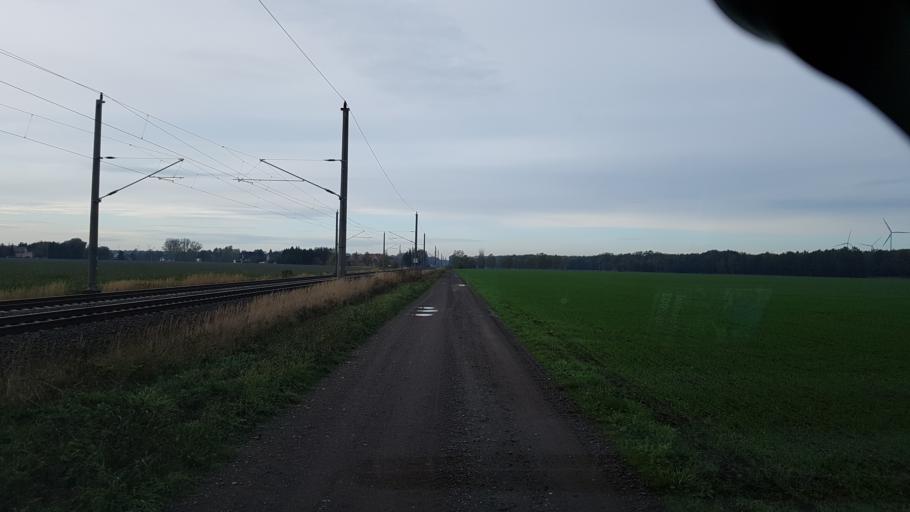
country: DE
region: Brandenburg
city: Falkenberg
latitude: 51.5525
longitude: 13.3048
